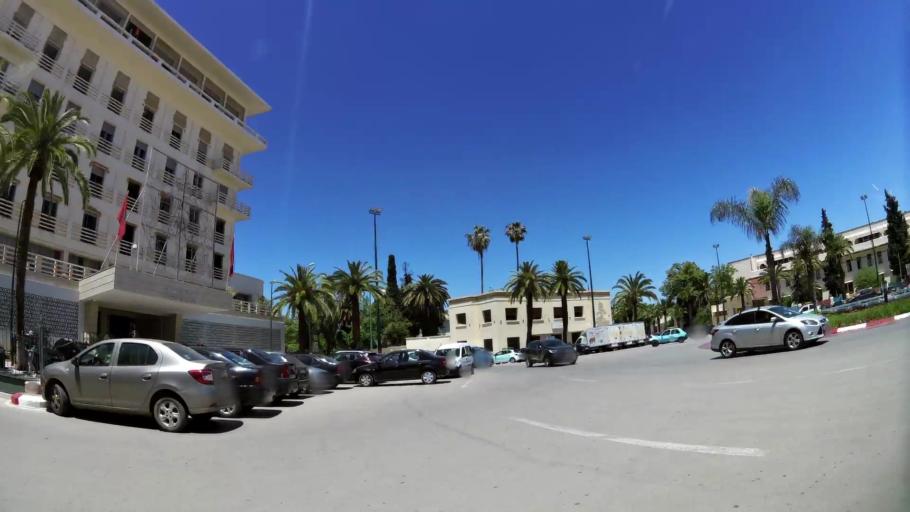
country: MA
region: Meknes-Tafilalet
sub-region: Meknes
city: Meknes
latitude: 33.9011
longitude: -5.5512
